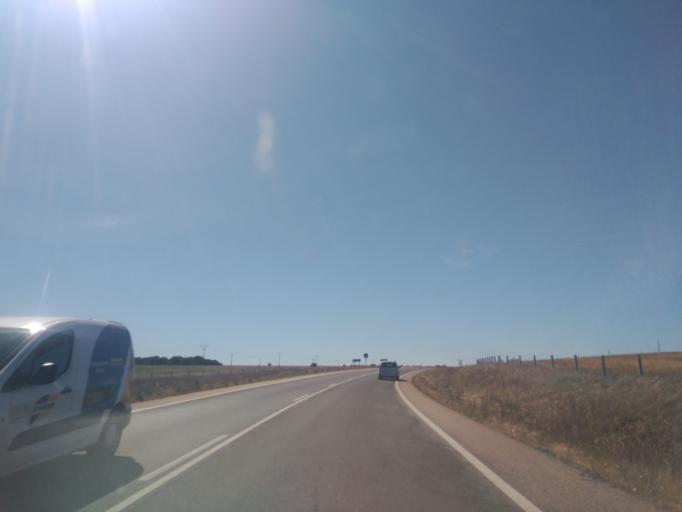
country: ES
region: Castille and Leon
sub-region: Provincia de Salamanca
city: Calvarrasa de Arriba
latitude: 40.9246
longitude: -5.6136
